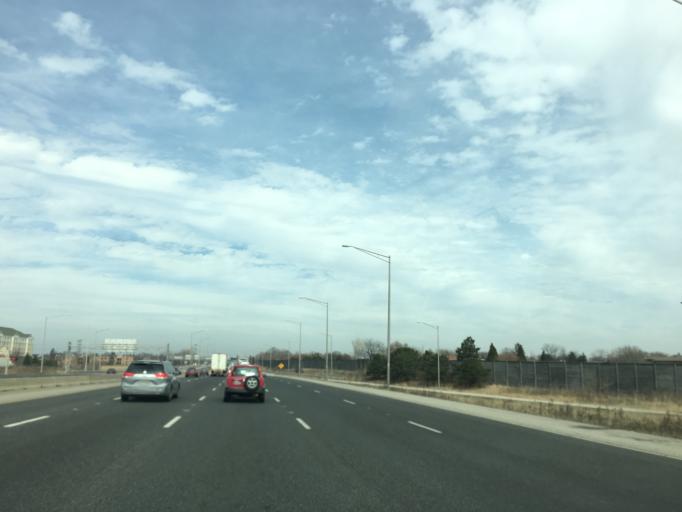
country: US
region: Illinois
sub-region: DuPage County
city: Glendale Heights
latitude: 41.9328
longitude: -88.0374
